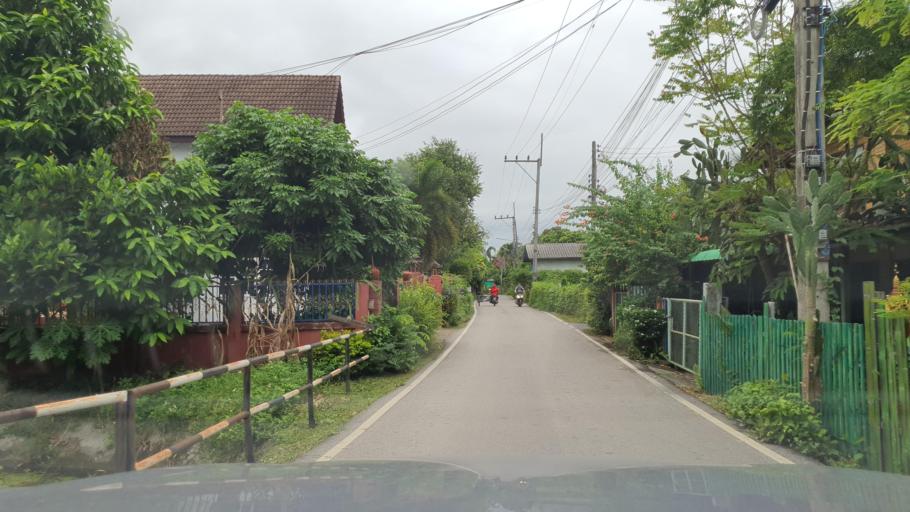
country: TH
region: Lamphun
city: Lamphun
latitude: 18.6008
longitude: 98.9727
